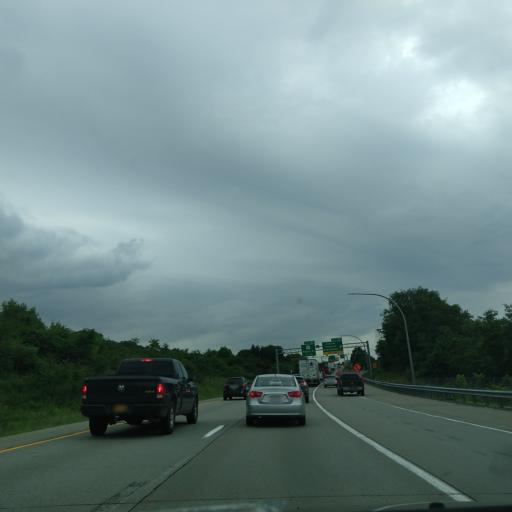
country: US
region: Pennsylvania
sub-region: Lackawanna County
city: Dunmore
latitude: 41.3976
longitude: -75.6410
